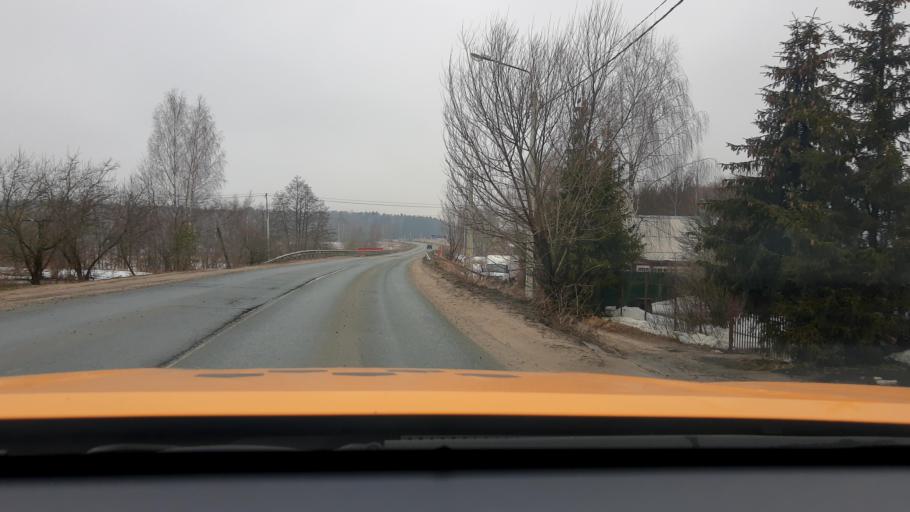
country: RU
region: Moskovskaya
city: Yamkino
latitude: 55.9352
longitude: 38.4224
